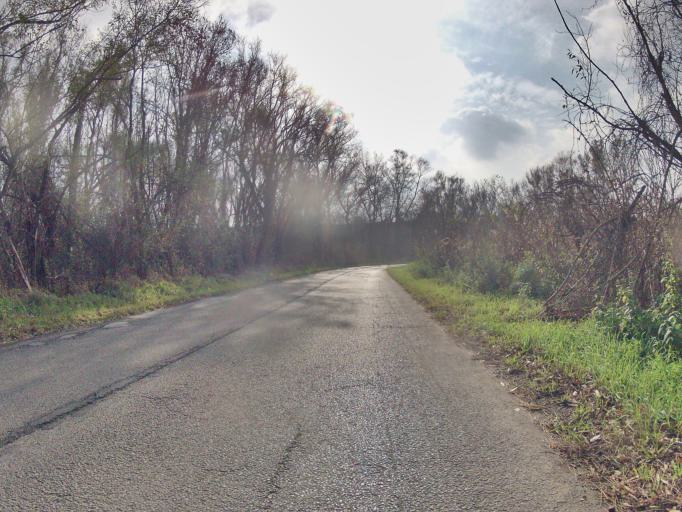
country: PL
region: Lesser Poland Voivodeship
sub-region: Powiat wielicki
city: Wegrzce Wielkie
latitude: 50.0659
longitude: 20.1096
